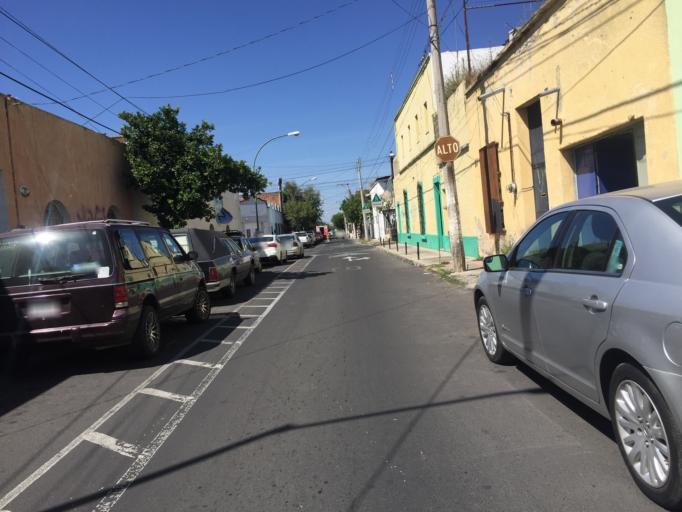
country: MX
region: Jalisco
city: Guadalajara
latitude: 20.6836
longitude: -103.3621
